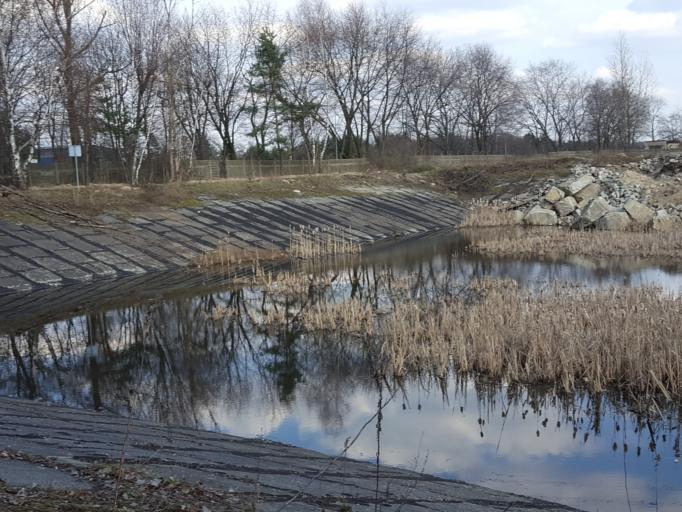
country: PL
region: Silesian Voivodeship
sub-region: Ruda Slaska
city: Ruda Slaska
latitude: 50.2346
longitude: 18.8462
